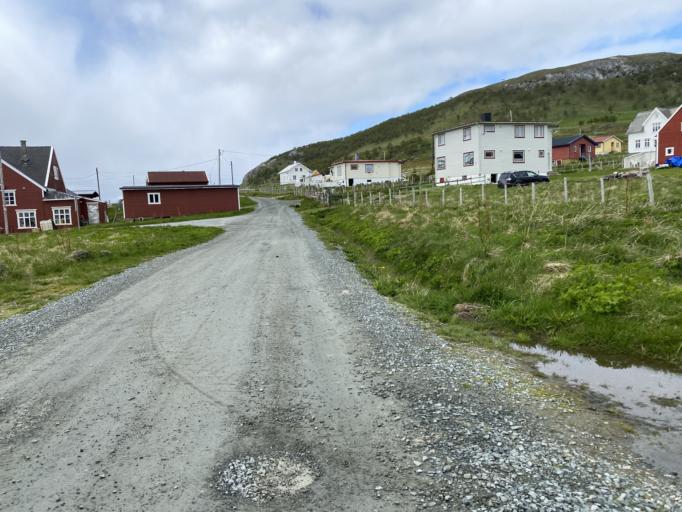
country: NO
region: Troms
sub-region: Karlsoy
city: Hansnes
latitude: 70.0023
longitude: 19.8908
